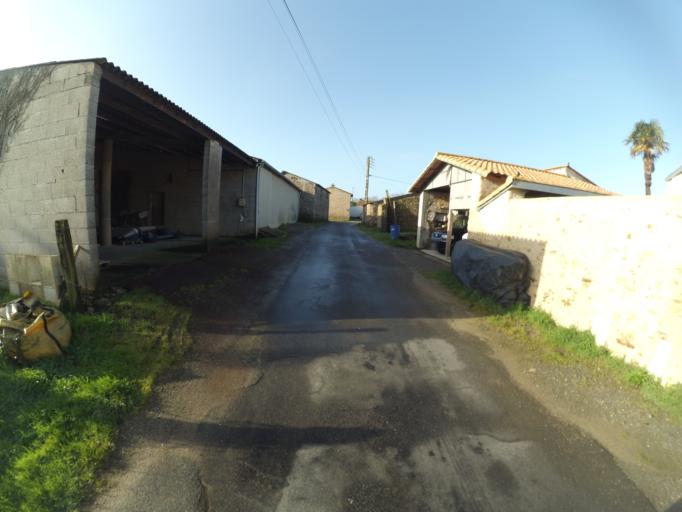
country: FR
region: Pays de la Loire
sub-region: Departement de la Loire-Atlantique
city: La Planche
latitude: 47.0224
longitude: -1.4555
